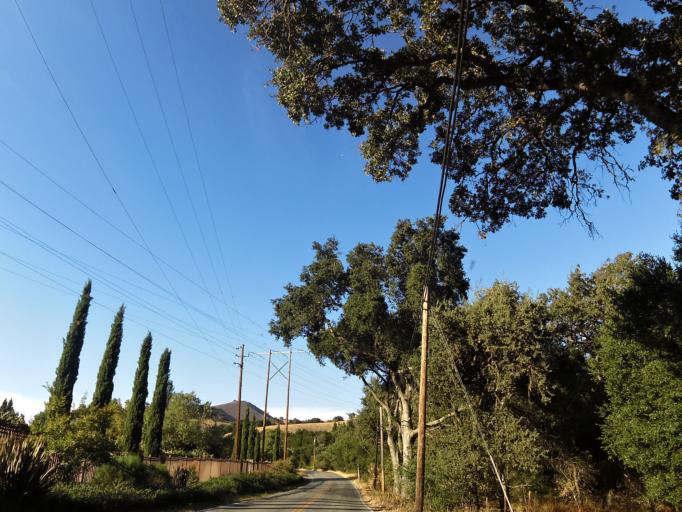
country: US
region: California
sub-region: Santa Clara County
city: Morgan Hill
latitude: 37.0999
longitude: -121.6727
